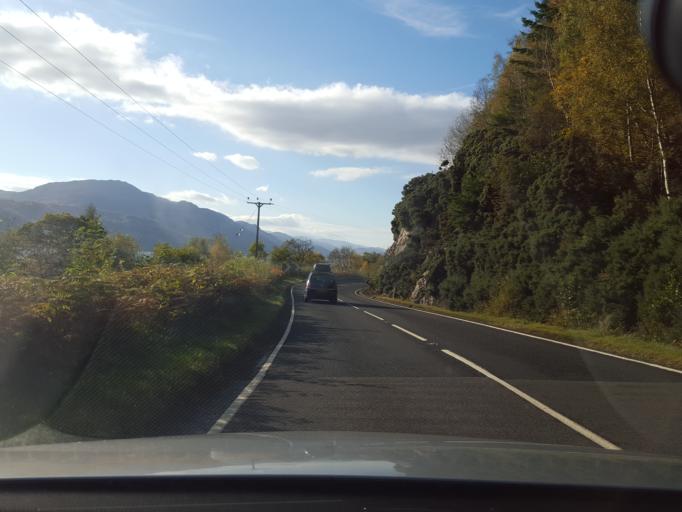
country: GB
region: Scotland
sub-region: Highland
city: Beauly
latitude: 57.2210
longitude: -4.5795
